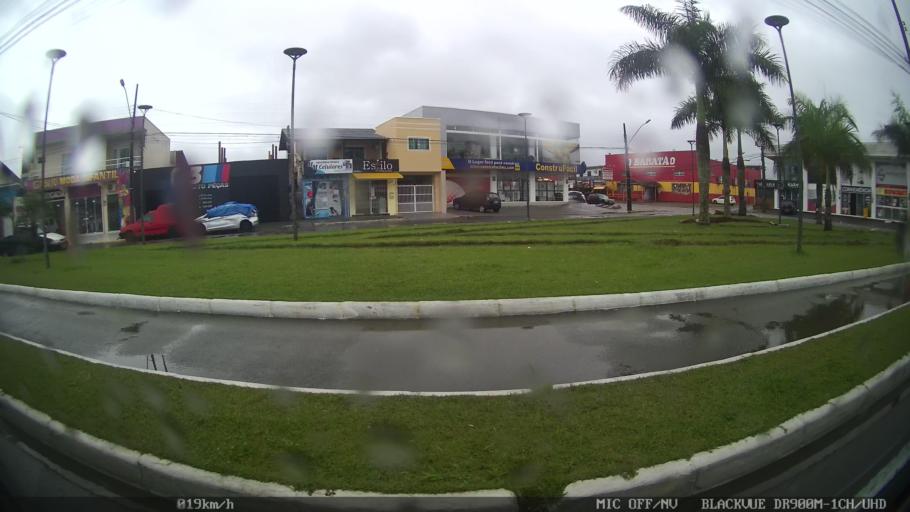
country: BR
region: Santa Catarina
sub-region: Itajai
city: Itajai
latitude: -26.9265
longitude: -48.6946
